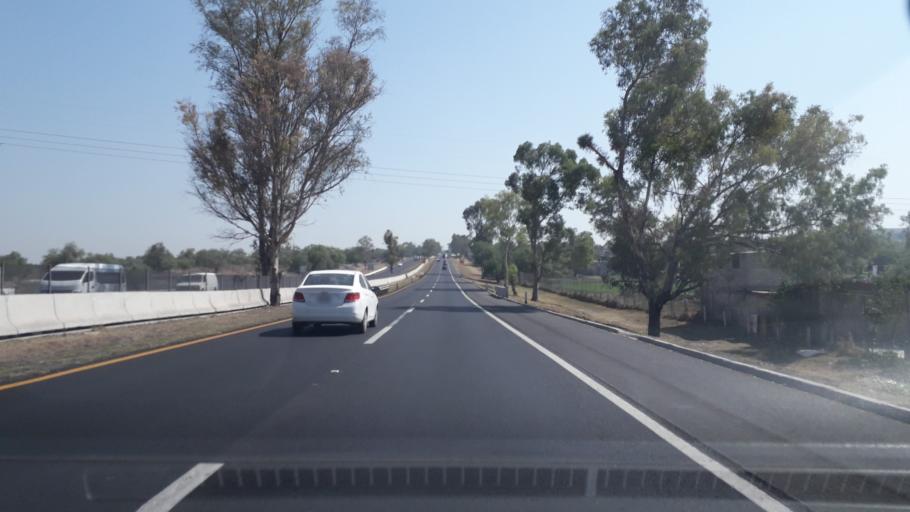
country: MX
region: Mexico
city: Santo Tomas Chiconautla
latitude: 19.6466
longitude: -99.0147
